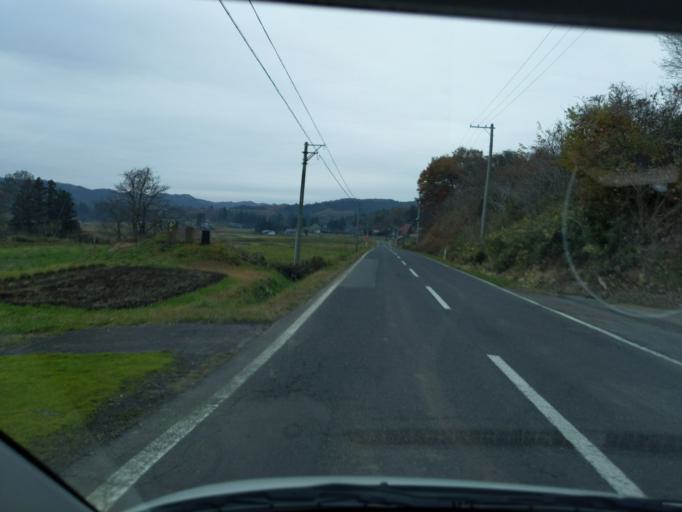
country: JP
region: Iwate
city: Kitakami
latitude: 39.2581
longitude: 141.2027
